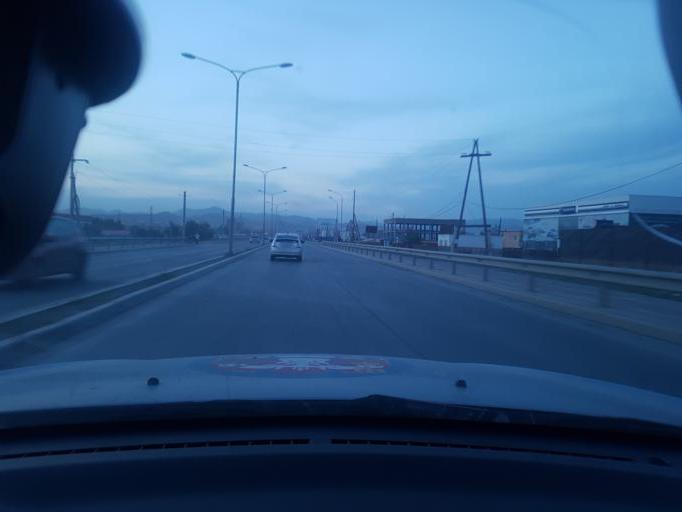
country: MN
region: Ulaanbaatar
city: Ulaanbaatar
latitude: 47.8973
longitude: 106.7856
